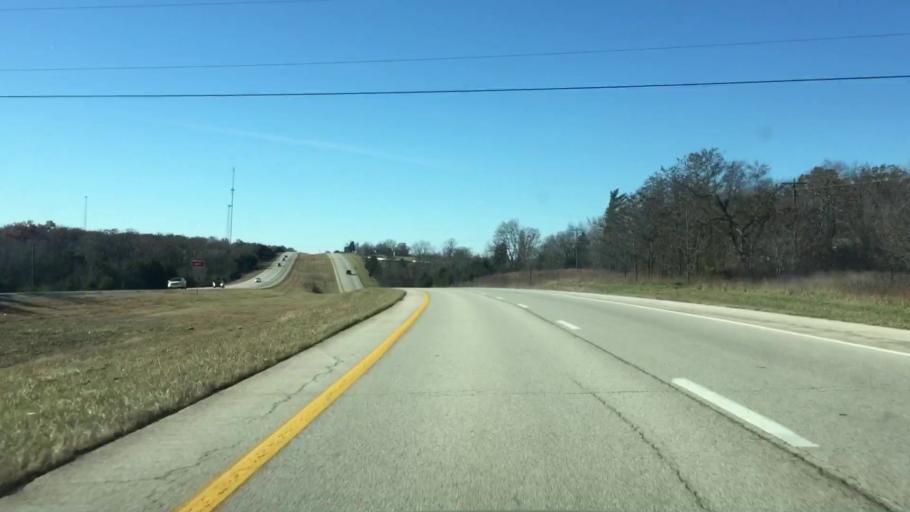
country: US
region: Missouri
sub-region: Cole County
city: Saint Martins
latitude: 38.4212
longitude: -92.3383
